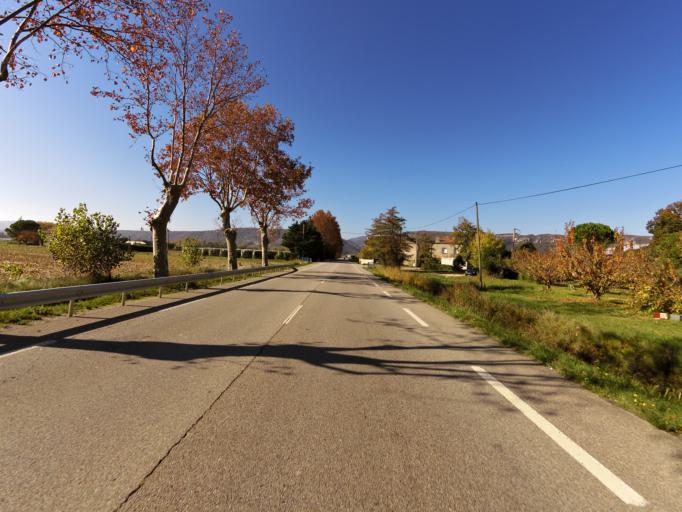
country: FR
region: Rhone-Alpes
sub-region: Departement de l'Ardeche
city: Le Pouzin
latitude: 44.7557
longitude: 4.7769
